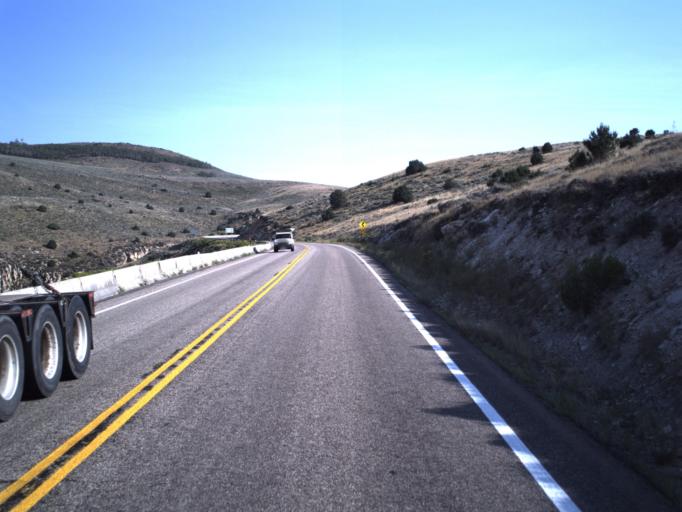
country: US
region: Utah
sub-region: Uintah County
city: Maeser
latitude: 40.6512
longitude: -109.4895
